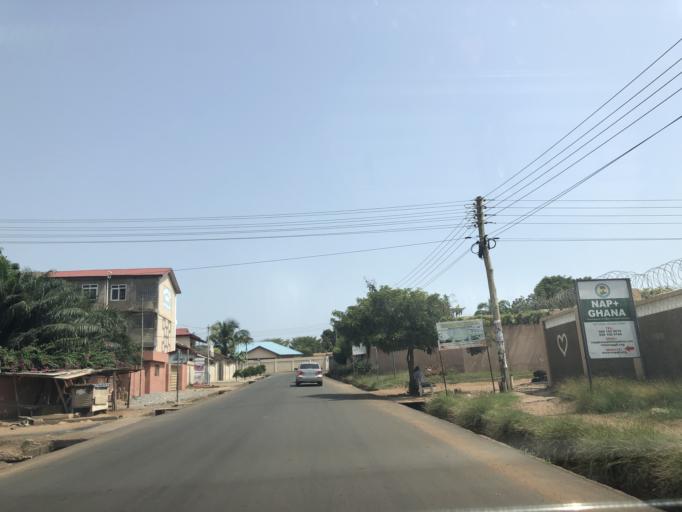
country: GH
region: Greater Accra
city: Dome
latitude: 5.6198
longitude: -0.2502
